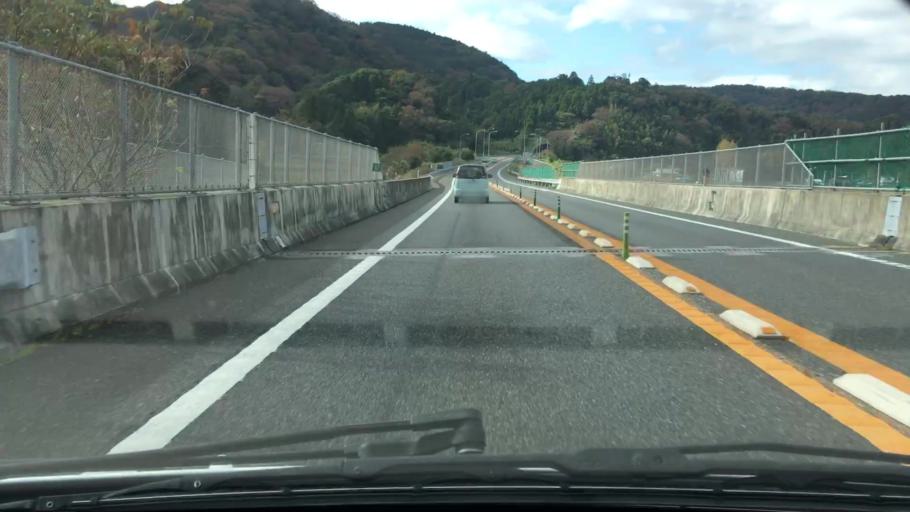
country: JP
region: Chiba
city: Futtsu
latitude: 35.1968
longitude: 139.8608
